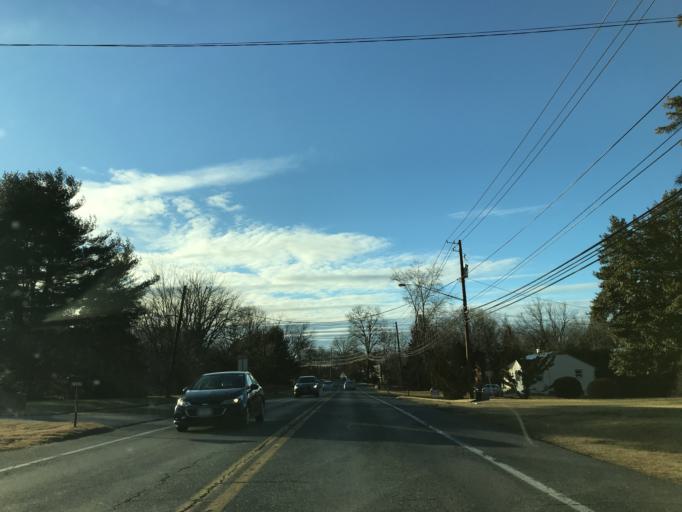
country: US
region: Maryland
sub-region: Montgomery County
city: Fairland
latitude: 39.0779
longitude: -76.9617
